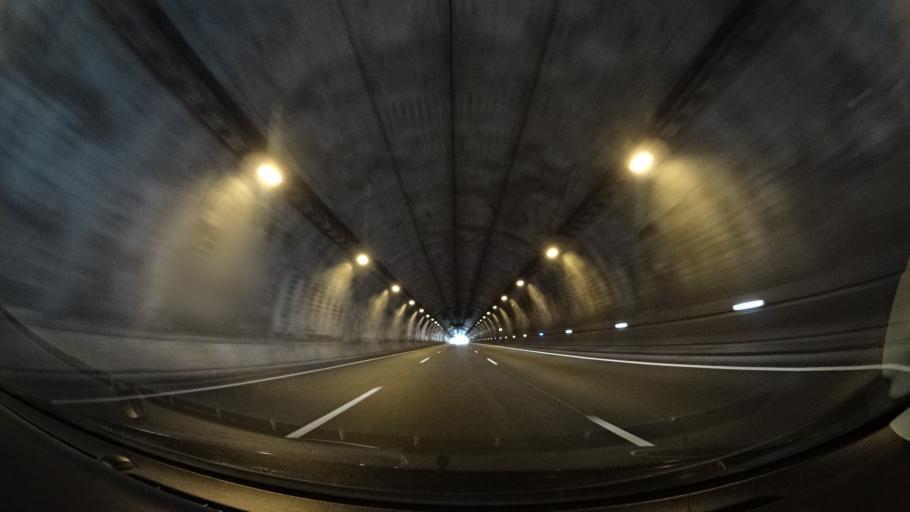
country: ES
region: Basque Country
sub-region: Provincia de Guipuzcoa
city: Errenteria
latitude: 43.2838
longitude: -1.9127
